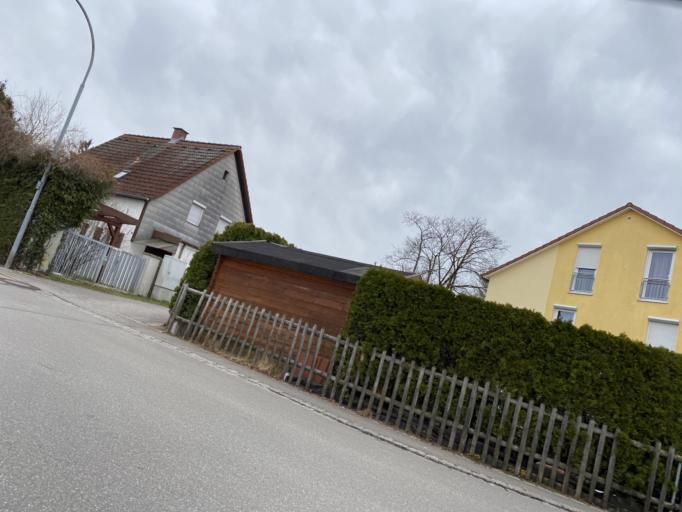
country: DE
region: Bavaria
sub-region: Upper Bavaria
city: Fuerstenfeldbruck
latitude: 48.1873
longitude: 11.2568
